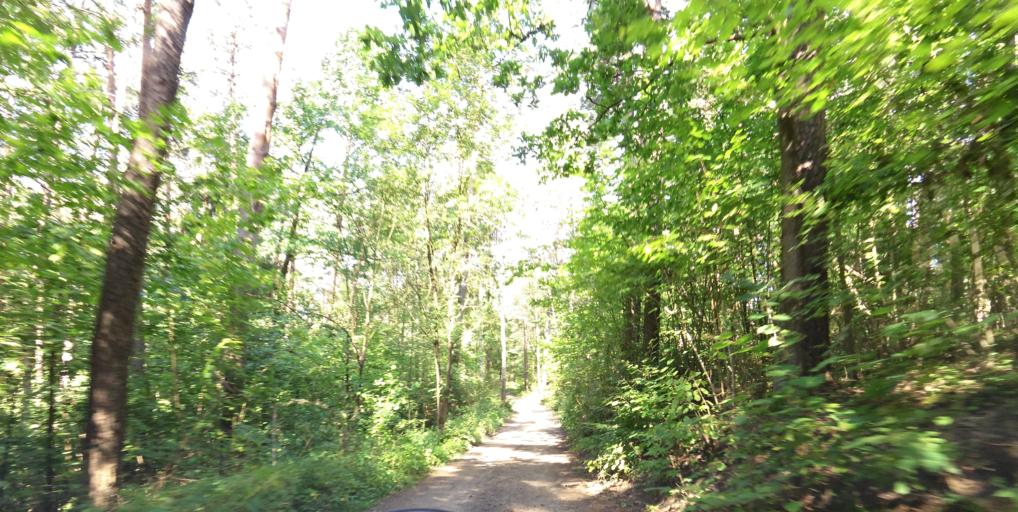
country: LT
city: Grigiskes
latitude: 54.7410
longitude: 25.0286
